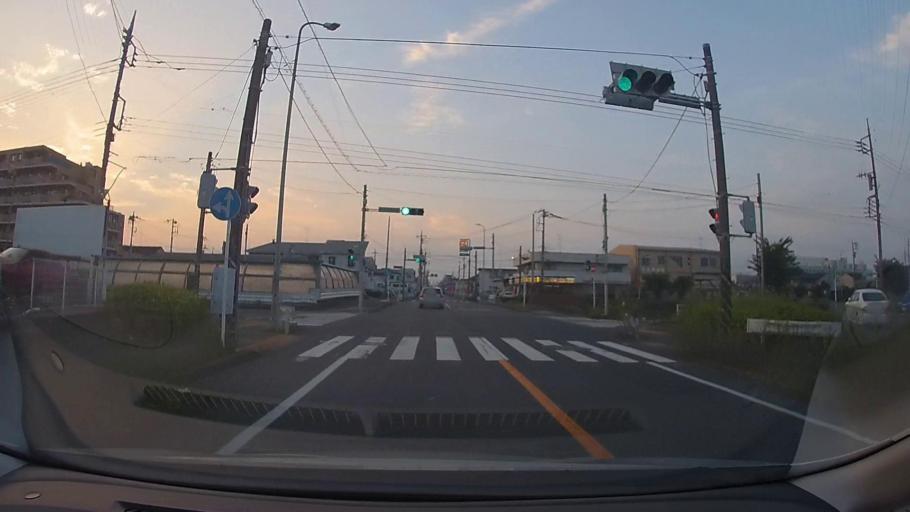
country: JP
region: Kanagawa
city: Minami-rinkan
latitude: 35.4810
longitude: 139.4521
